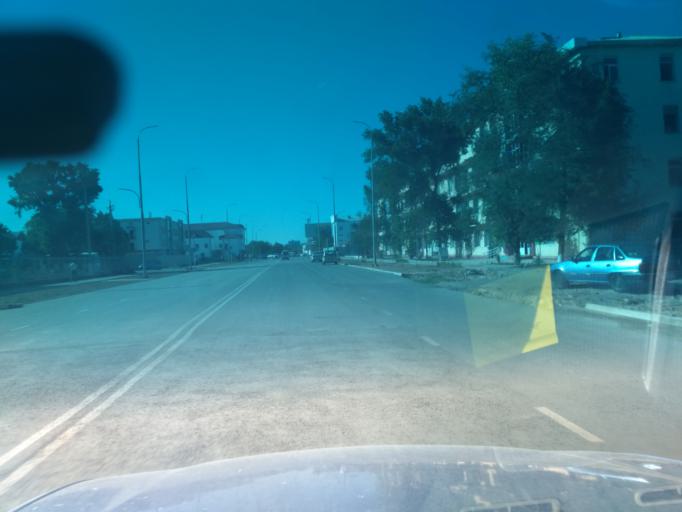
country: UZ
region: Sirdaryo
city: Guliston
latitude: 40.4943
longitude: 68.7717
